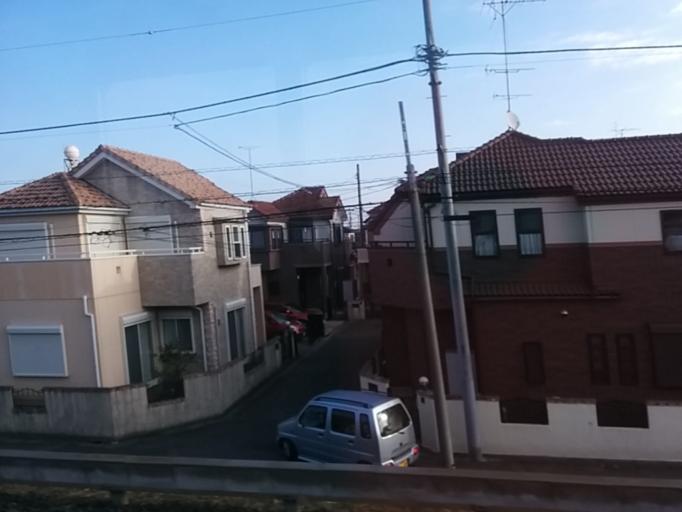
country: JP
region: Saitama
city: Kawagoe
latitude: 35.8975
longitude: 139.4915
